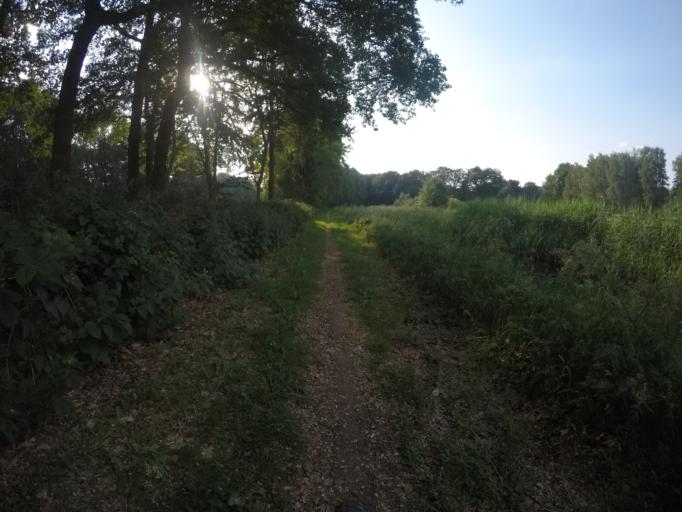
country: DE
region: North Rhine-Westphalia
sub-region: Regierungsbezirk Munster
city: Isselburg
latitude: 51.8375
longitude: 6.4361
